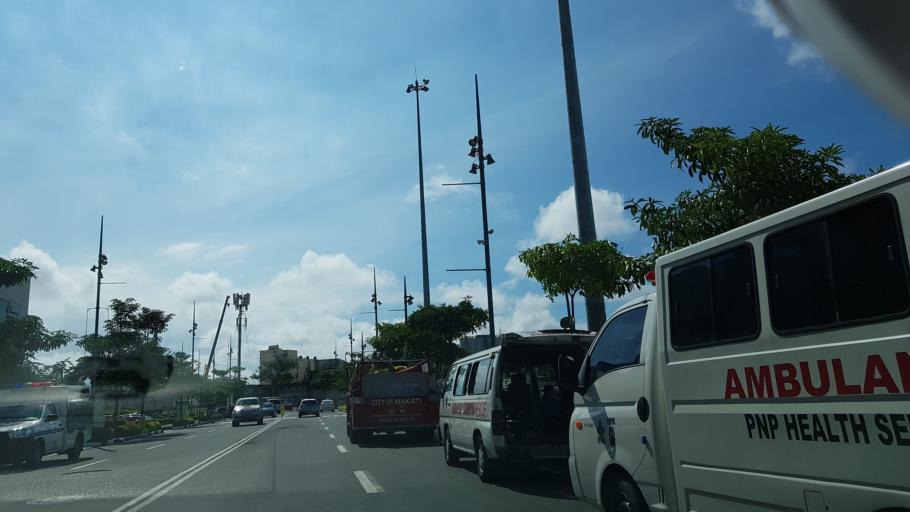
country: PH
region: Metro Manila
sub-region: Mandaluyong
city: Mandaluyong City
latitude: 14.5764
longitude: 121.0198
